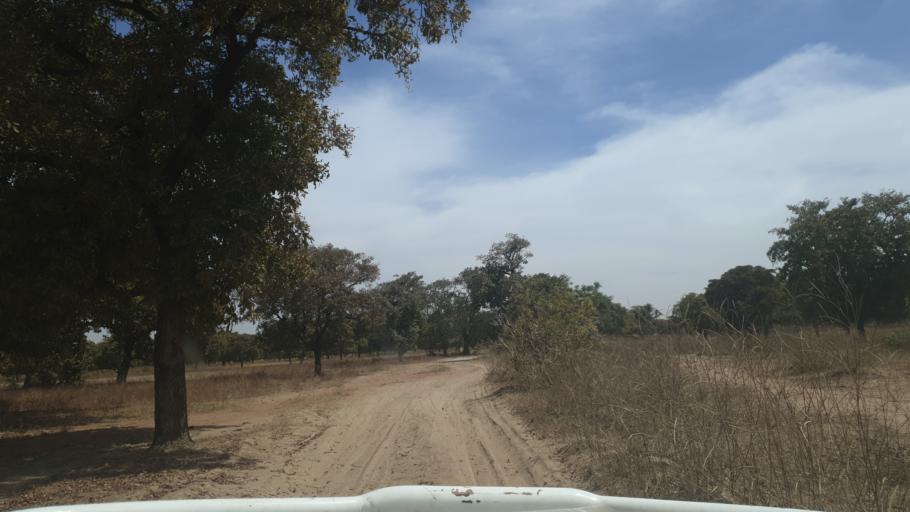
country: ML
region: Sikasso
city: Yorosso
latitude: 12.2919
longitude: -4.6650
